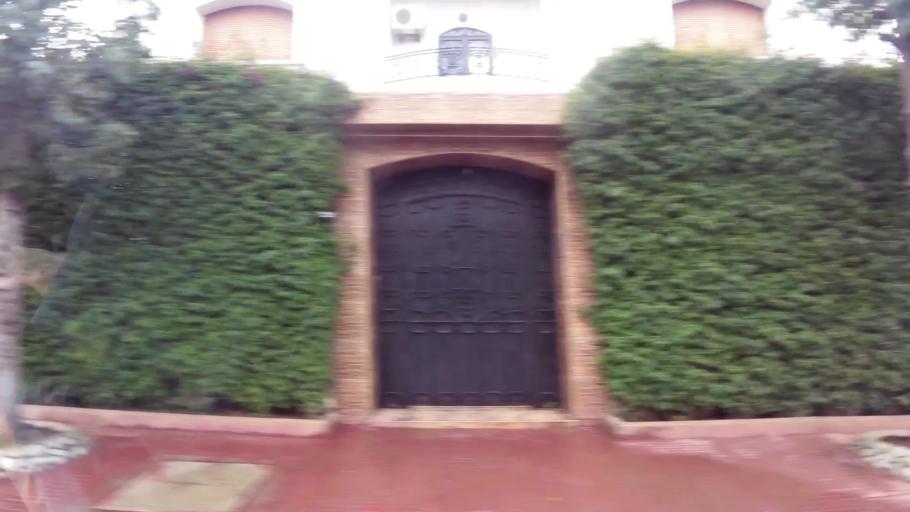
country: MA
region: Grand Casablanca
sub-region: Nouaceur
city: Bouskoura
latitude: 33.5159
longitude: -7.6435
